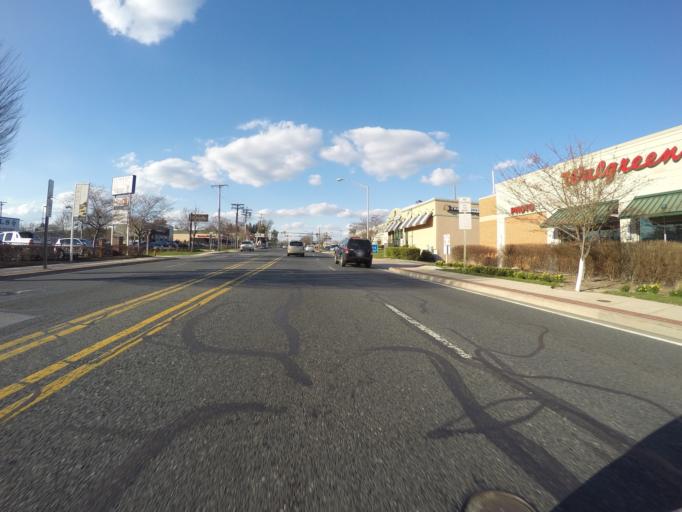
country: US
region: Maryland
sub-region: Baltimore County
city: Towson
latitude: 39.3708
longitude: -76.6098
